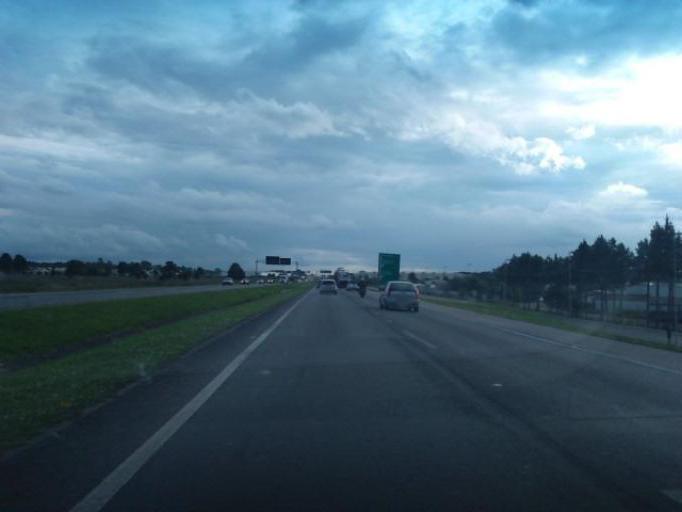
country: BR
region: Parana
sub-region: Piraquara
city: Piraquara
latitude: -25.5031
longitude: -49.1219
